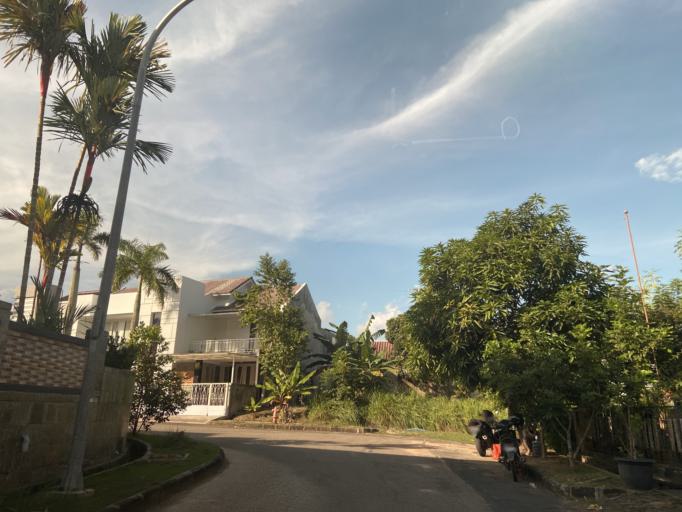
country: SG
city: Singapore
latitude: 1.1044
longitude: 104.0251
